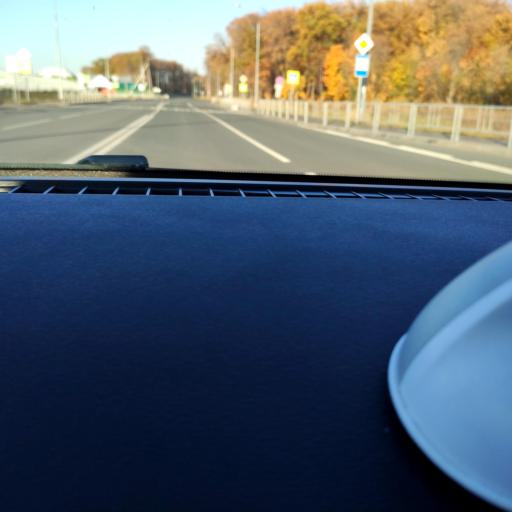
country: RU
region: Samara
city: Petra-Dubrava
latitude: 53.2923
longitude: 50.2404
